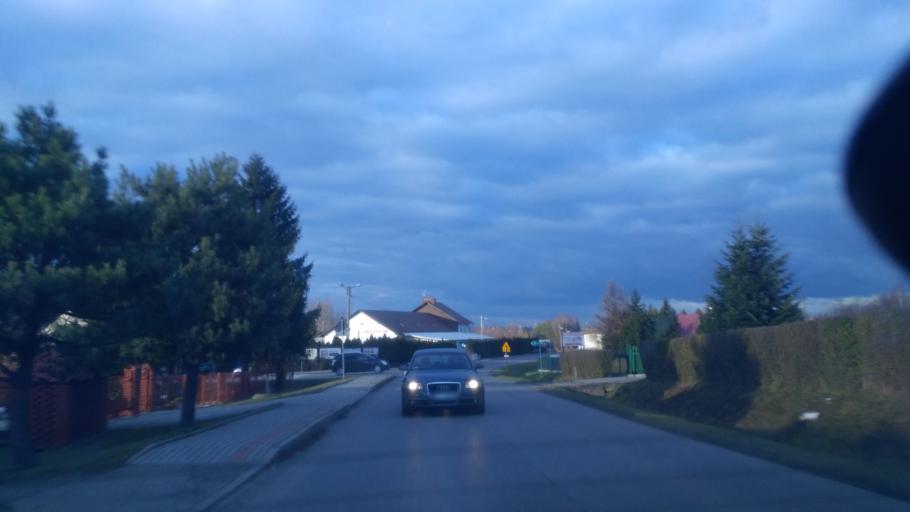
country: PL
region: Subcarpathian Voivodeship
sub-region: Powiat rzeszowski
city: Krasne
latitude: 50.0606
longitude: 22.1189
